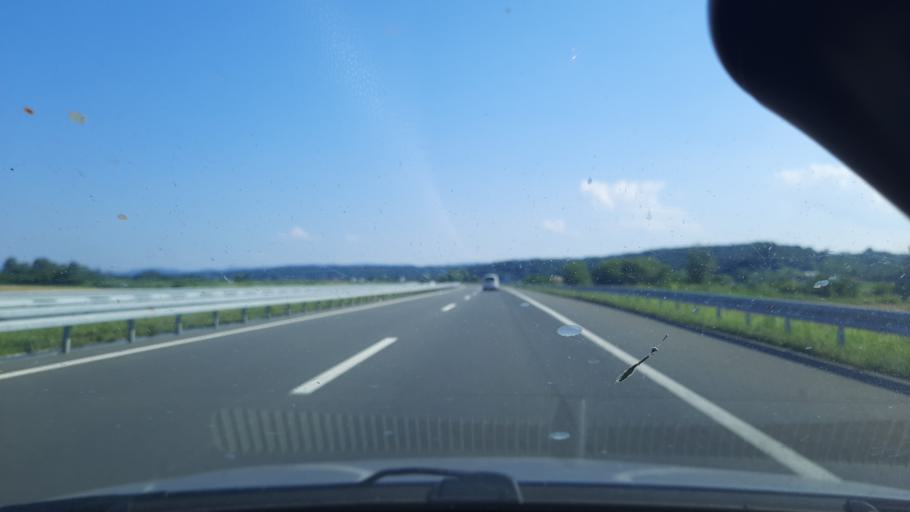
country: RS
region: Central Serbia
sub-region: Kolubarski Okrug
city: Lajkovac
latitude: 44.3241
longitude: 20.2126
